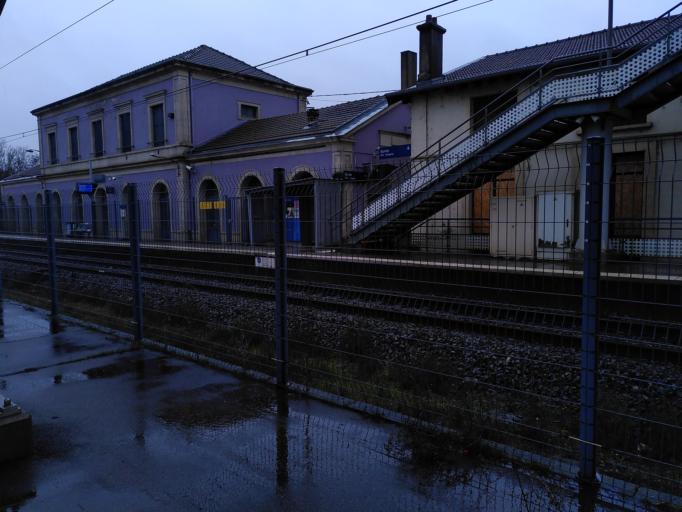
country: FR
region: Lorraine
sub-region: Departement de Meurthe-et-Moselle
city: Frouard
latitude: 48.7557
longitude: 6.1443
